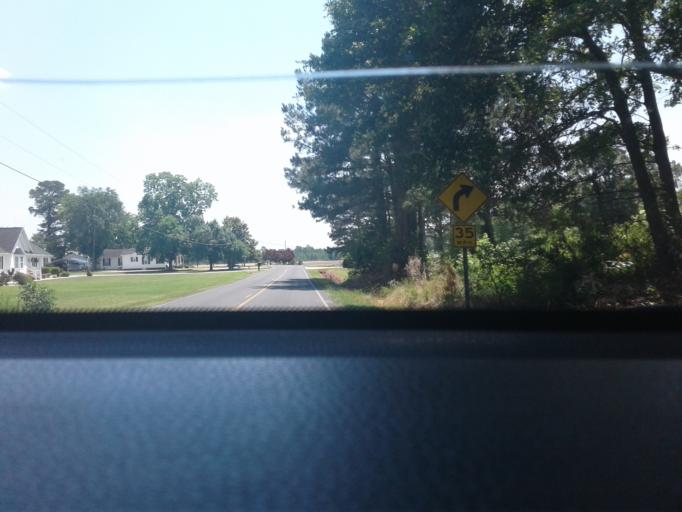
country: US
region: North Carolina
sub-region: Harnett County
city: Dunn
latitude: 35.3411
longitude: -78.5772
